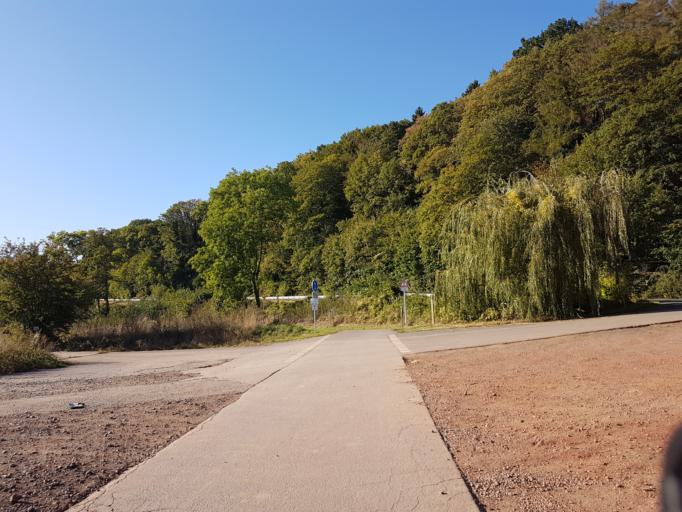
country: DE
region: North Rhine-Westphalia
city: Porta Westfalica
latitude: 52.2413
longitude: 8.8850
